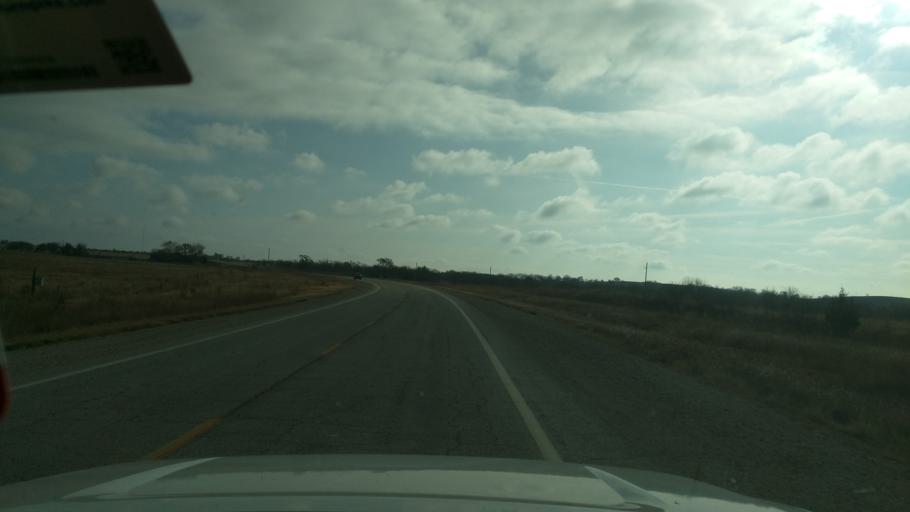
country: US
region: Kansas
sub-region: Chautauqua County
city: Sedan
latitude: 37.0844
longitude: -96.2181
